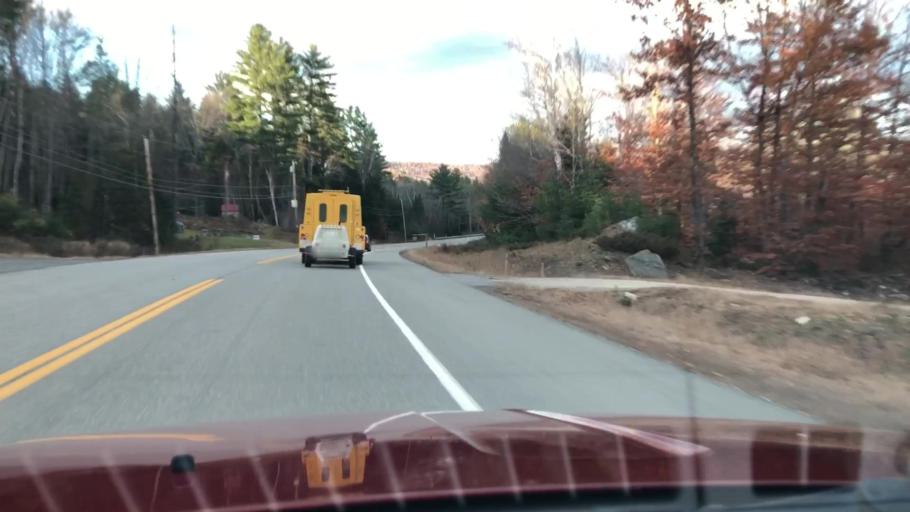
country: US
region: Maine
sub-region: Oxford County
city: Peru
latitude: 44.5336
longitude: -70.4061
